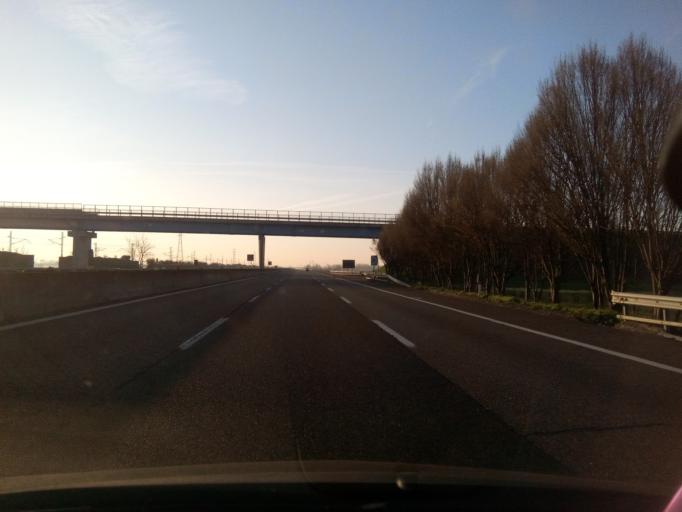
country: IT
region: Lombardy
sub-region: Provincia di Lodi
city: Senna Lodigiana
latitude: 45.1643
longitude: 9.6035
